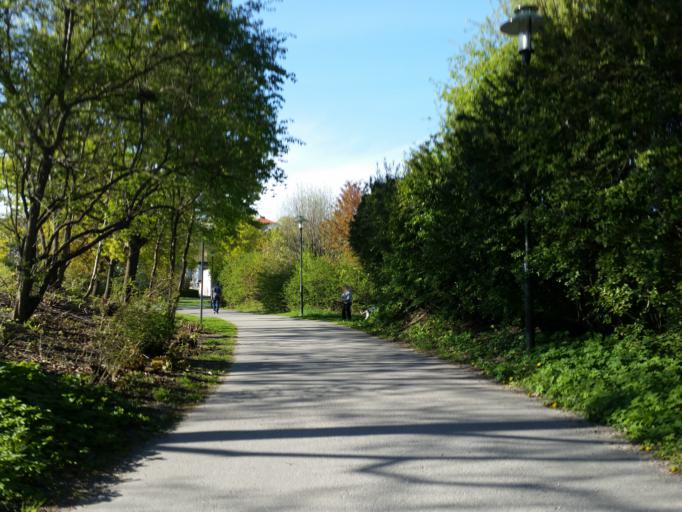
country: SE
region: Stockholm
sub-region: Stockholms Kommun
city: Arsta
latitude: 59.2890
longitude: 18.1010
